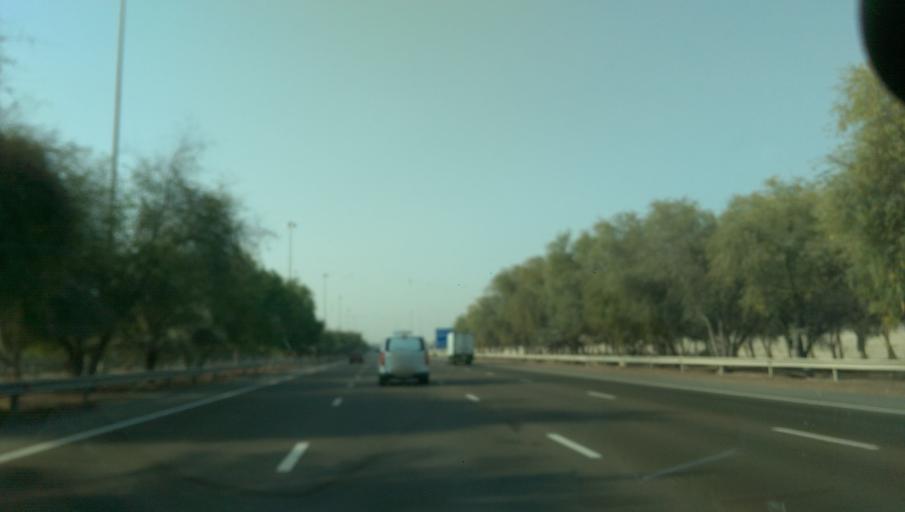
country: AE
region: Abu Dhabi
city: Abu Dhabi
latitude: 24.4714
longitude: 54.6763
